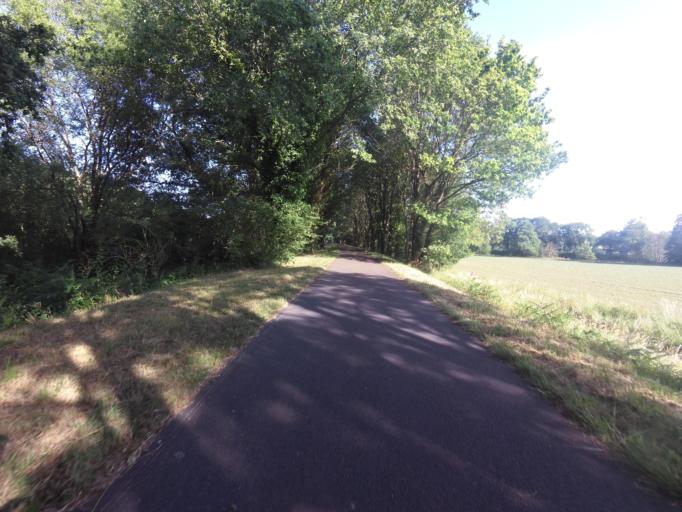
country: FR
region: Brittany
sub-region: Departement du Morbihan
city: Malestroit
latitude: 47.8415
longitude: -2.4347
